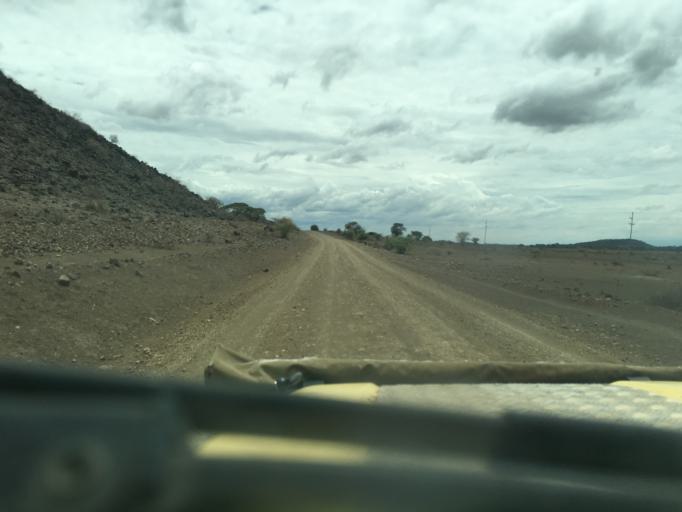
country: TZ
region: Arusha
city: Mto wa Mbu
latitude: -3.2360
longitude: 35.9461
